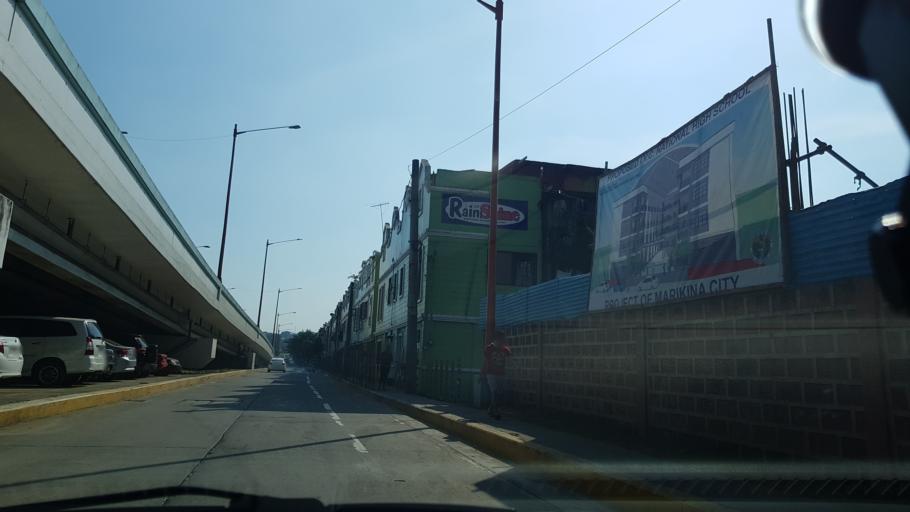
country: PH
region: Metro Manila
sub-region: Marikina
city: Calumpang
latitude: 14.6214
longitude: 121.0803
